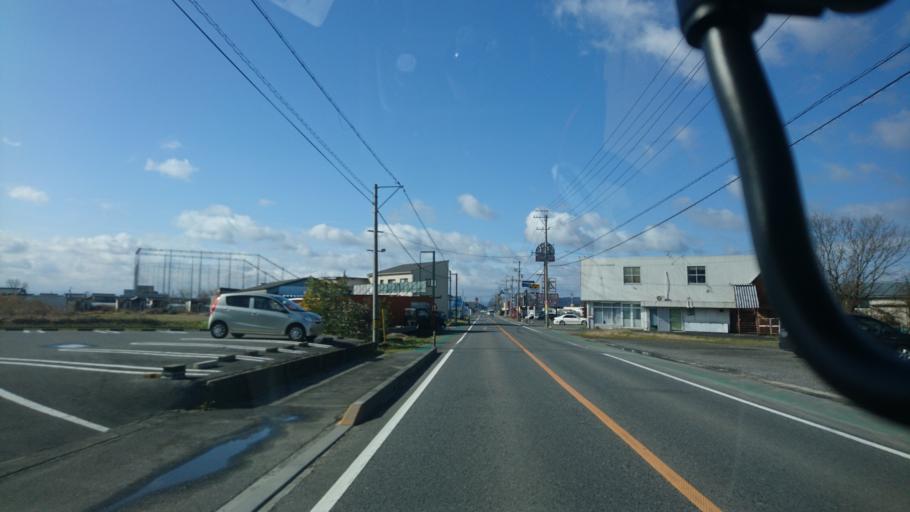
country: JP
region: Mie
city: Ueno-ebisumachi
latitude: 34.7852
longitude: 136.1387
